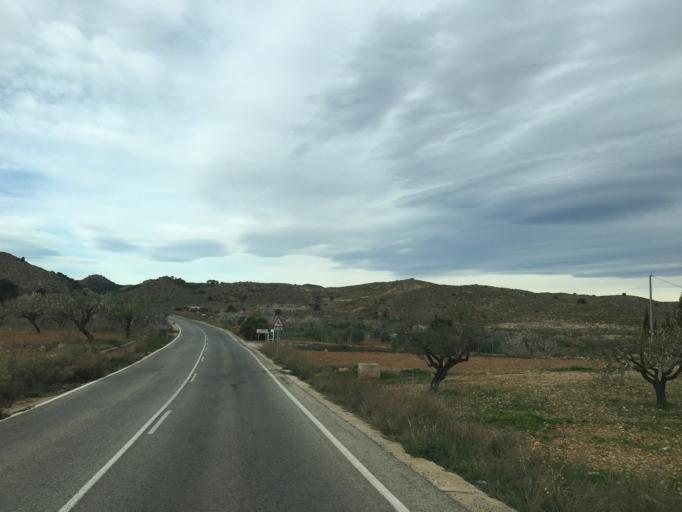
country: ES
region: Murcia
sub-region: Murcia
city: Fuente-Alamo de Murcia
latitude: 37.6125
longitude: -1.1004
